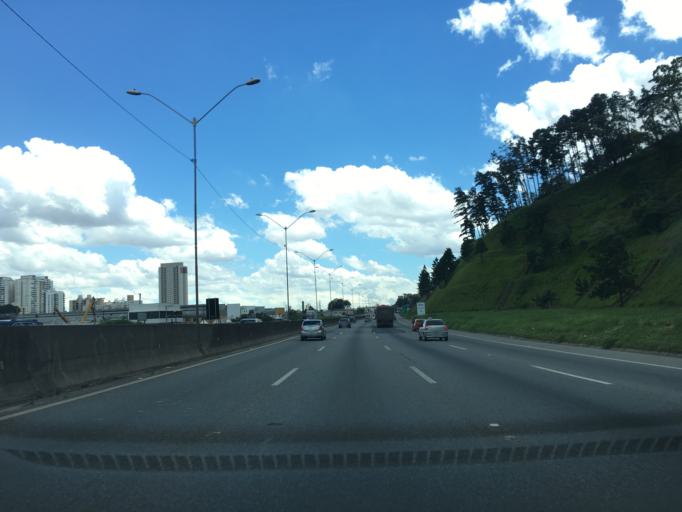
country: BR
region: Sao Paulo
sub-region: Guarulhos
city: Guarulhos
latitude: -23.4427
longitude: -46.5682
